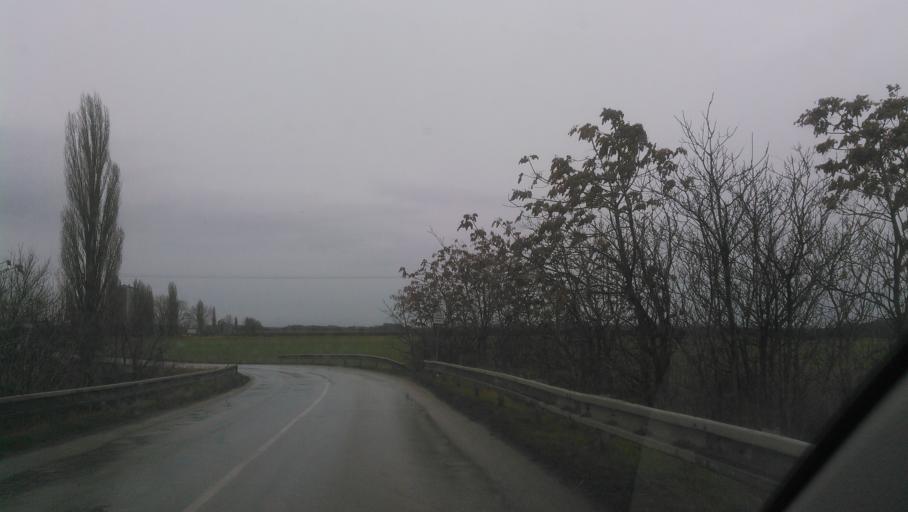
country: SK
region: Nitriansky
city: Sellye
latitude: 48.1433
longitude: 17.8806
